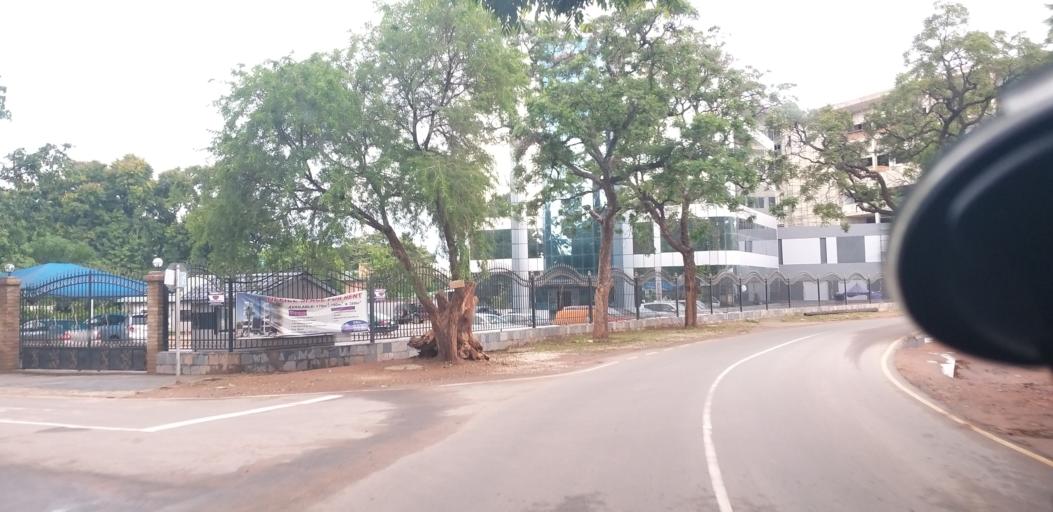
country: ZM
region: Lusaka
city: Lusaka
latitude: -15.4146
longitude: 28.3015
